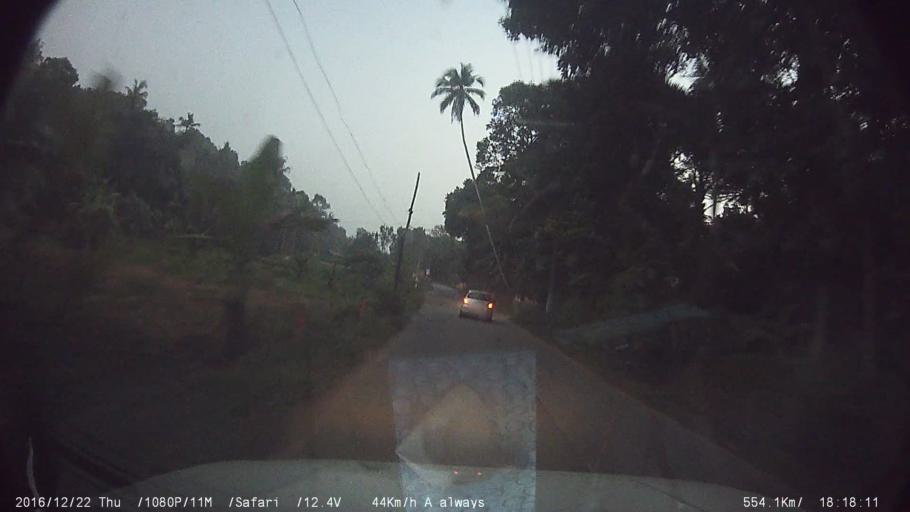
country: IN
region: Kerala
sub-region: Kottayam
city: Palackattumala
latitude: 9.7562
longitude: 76.6088
